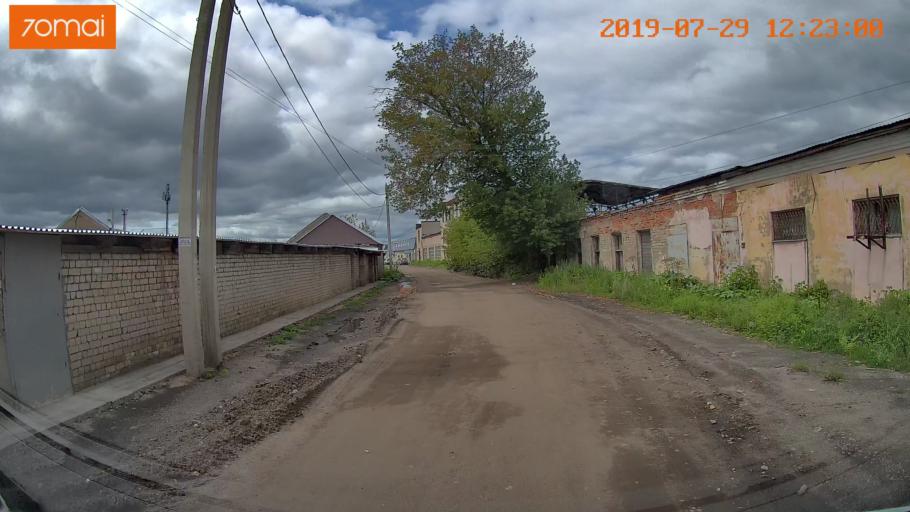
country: RU
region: Ivanovo
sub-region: Gorod Ivanovo
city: Ivanovo
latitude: 57.0057
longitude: 40.9389
